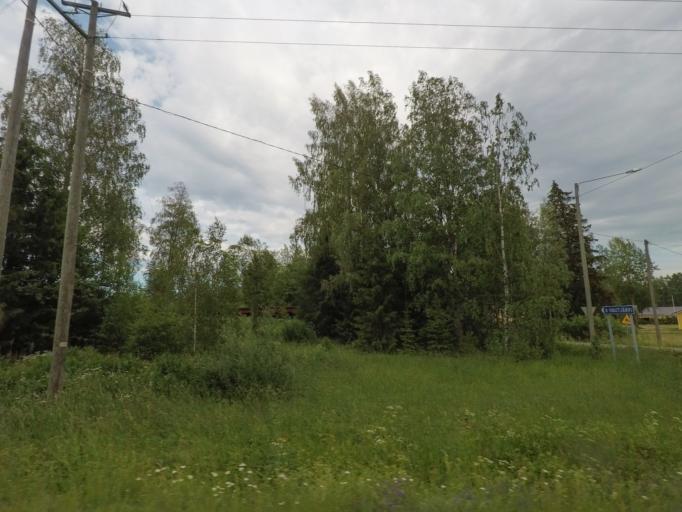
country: FI
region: Uusimaa
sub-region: Porvoo
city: Pukkila
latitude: 60.7625
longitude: 25.4430
